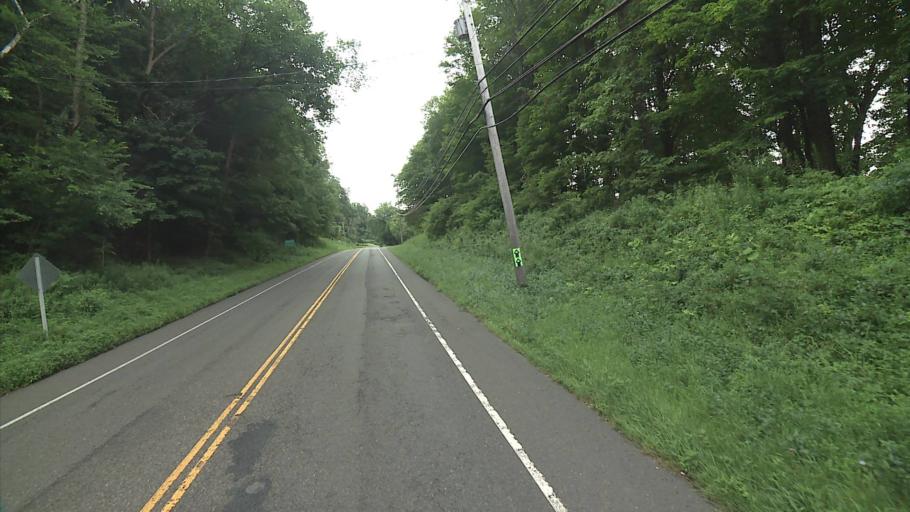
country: US
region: Connecticut
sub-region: Litchfield County
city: New Milford
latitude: 41.5580
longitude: -73.3887
